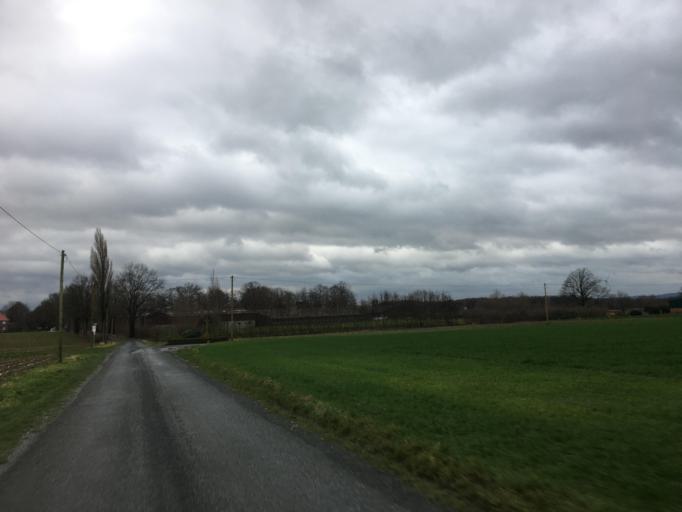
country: DE
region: North Rhine-Westphalia
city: Olfen
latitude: 51.7552
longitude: 7.3493
